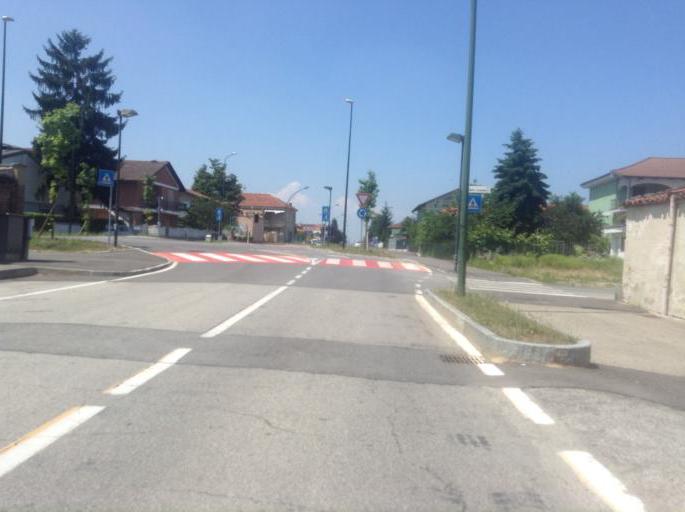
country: IT
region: Piedmont
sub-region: Provincia di Torino
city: Carignano
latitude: 44.9130
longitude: 7.6773
